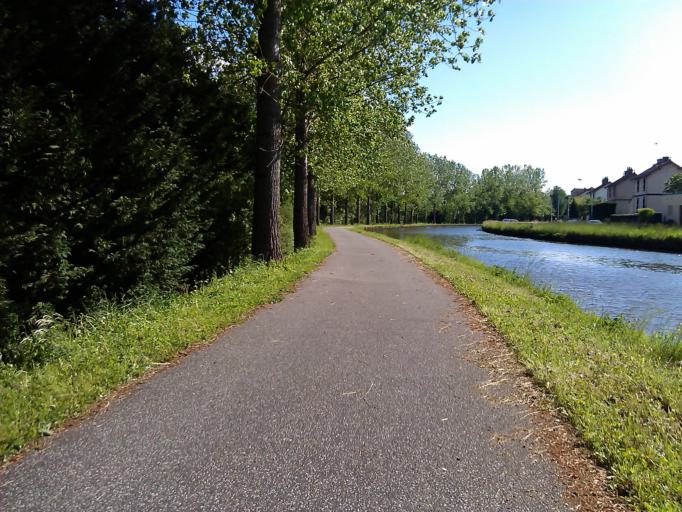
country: FR
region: Bourgogne
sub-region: Departement de Saone-et-Loire
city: Ecuisses
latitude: 46.7656
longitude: 4.5243
